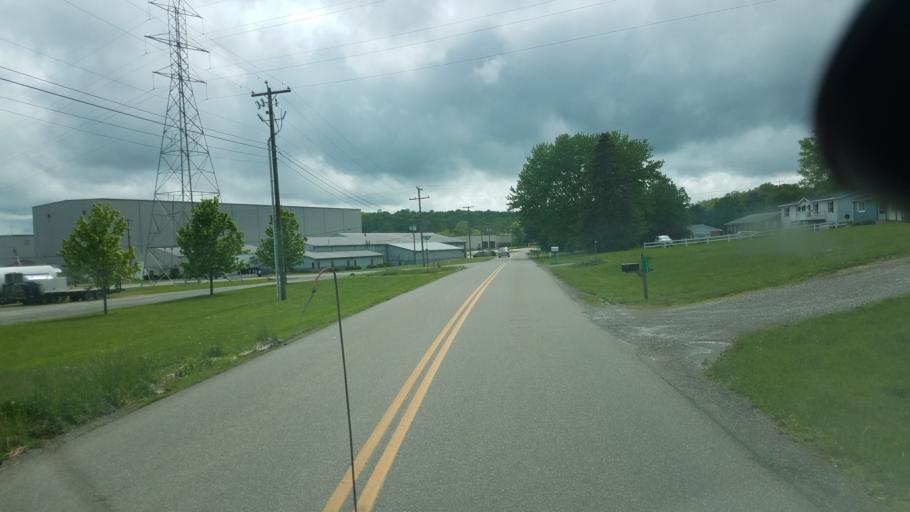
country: US
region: Ohio
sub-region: Tuscarawas County
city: Strasburg
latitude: 40.6447
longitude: -81.4610
